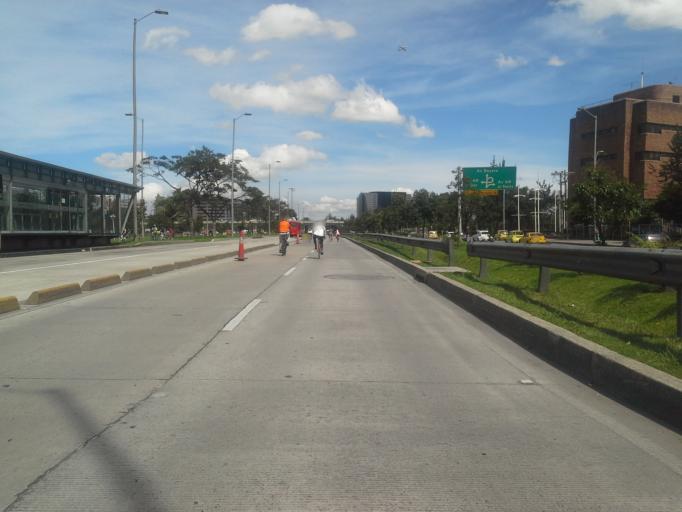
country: CO
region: Bogota D.C.
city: Bogota
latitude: 4.6511
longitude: -74.1016
